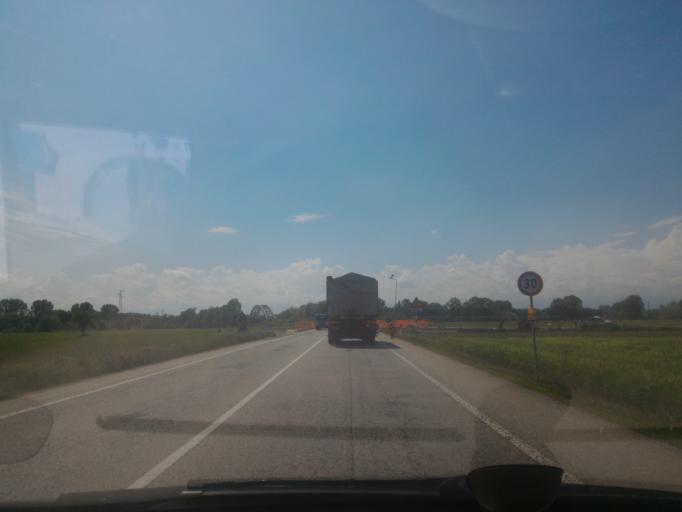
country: IT
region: Piedmont
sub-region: Provincia di Torino
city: Carignano
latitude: 44.9116
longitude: 7.6967
